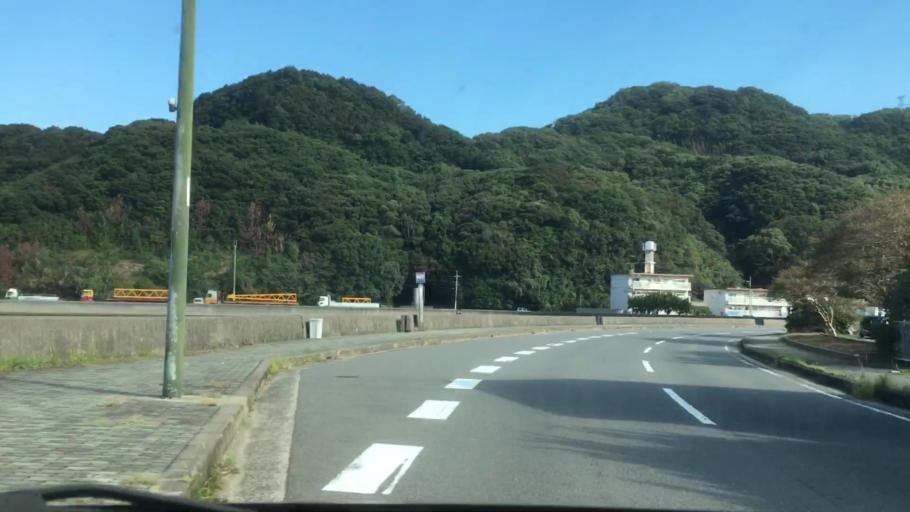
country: JP
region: Nagasaki
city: Sasebo
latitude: 32.9464
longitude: 129.6378
